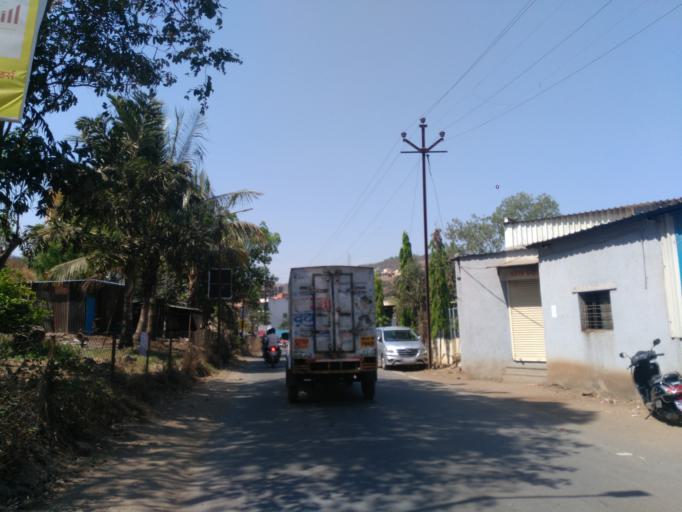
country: IN
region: Maharashtra
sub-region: Pune Division
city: Pune
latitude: 18.4400
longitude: 73.8637
